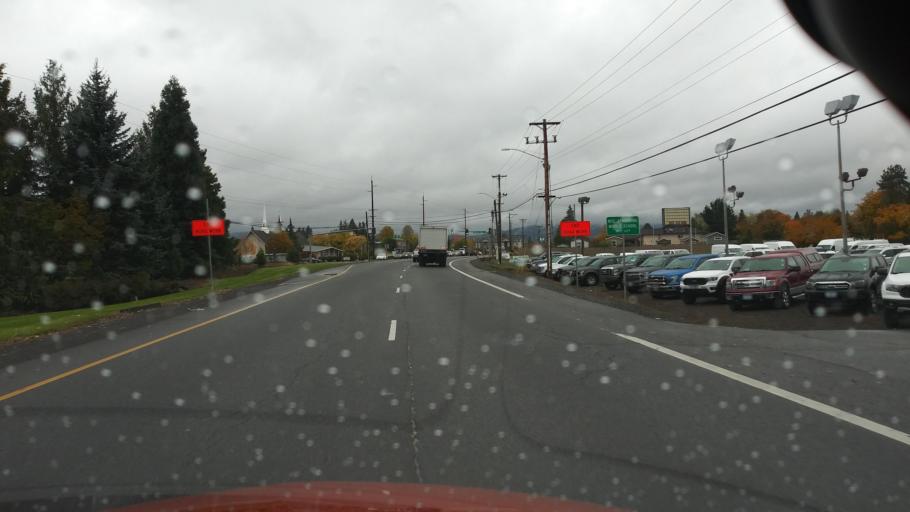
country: US
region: Oregon
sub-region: Washington County
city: Cornelius
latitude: 45.5206
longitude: -123.0738
